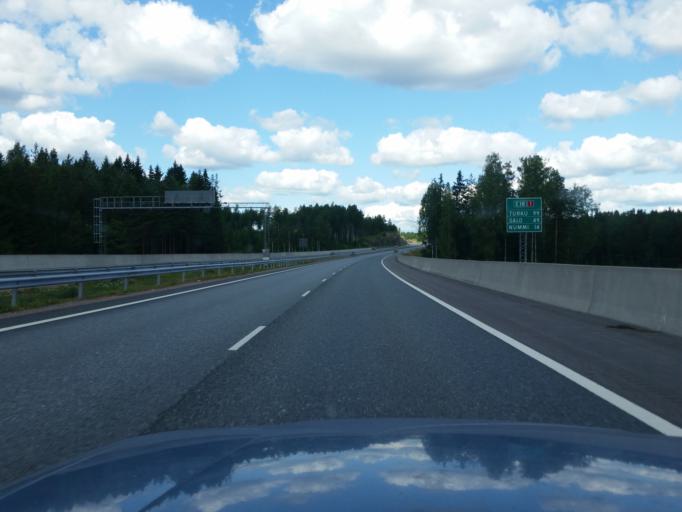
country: FI
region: Uusimaa
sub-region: Helsinki
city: Sammatti
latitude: 60.3509
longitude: 23.8967
